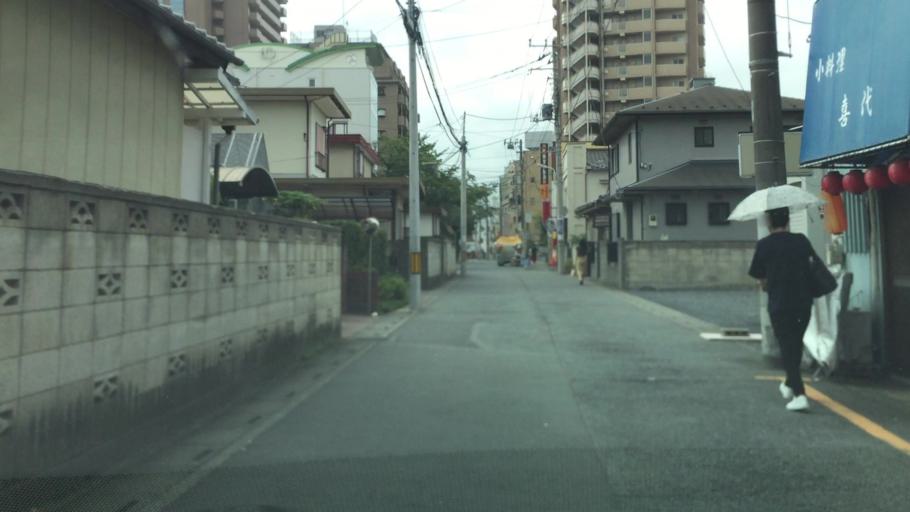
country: JP
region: Saitama
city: Ageoshimo
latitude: 35.9420
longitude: 139.6093
